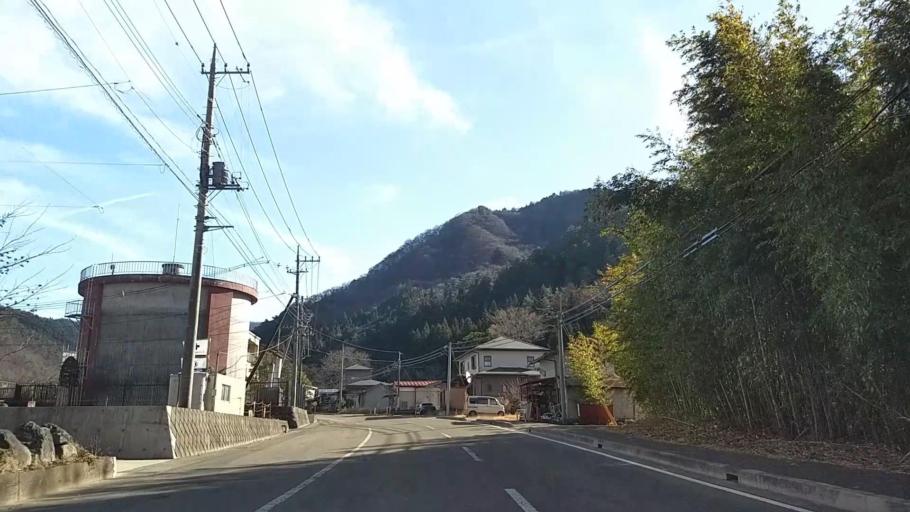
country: JP
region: Yamanashi
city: Otsuki
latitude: 35.5301
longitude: 138.9170
